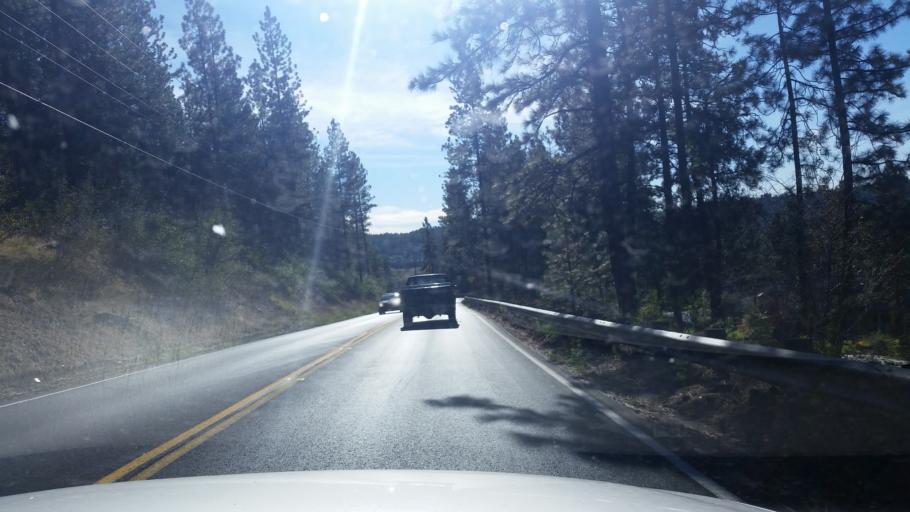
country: US
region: Washington
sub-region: Spokane County
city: Spokane
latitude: 47.5974
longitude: -117.3904
